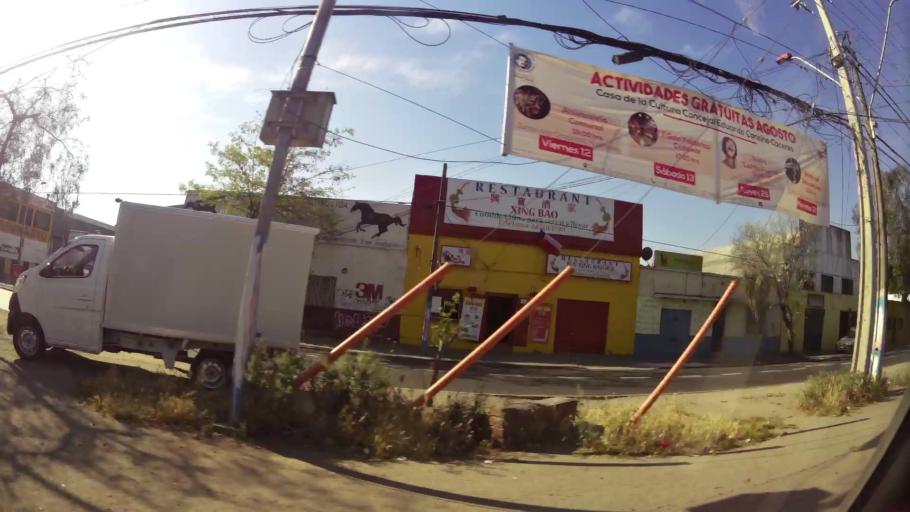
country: CL
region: Santiago Metropolitan
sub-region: Provincia de Santiago
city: Santiago
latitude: -33.4788
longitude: -70.6621
